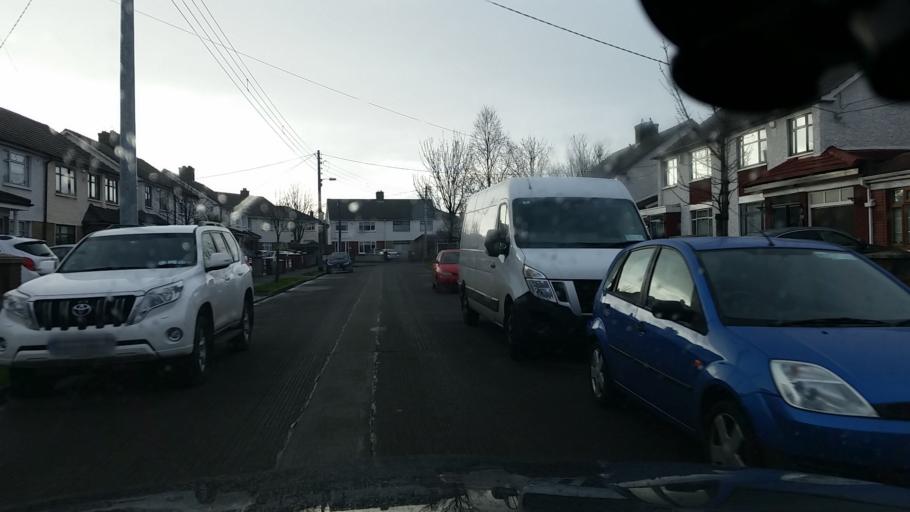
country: IE
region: Leinster
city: Artane
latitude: 53.3899
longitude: -6.2123
